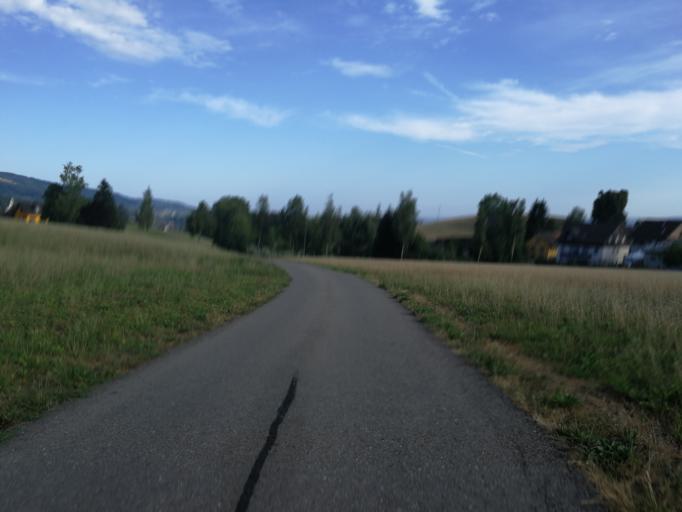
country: CH
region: Zurich
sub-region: Bezirk Meilen
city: Oetwil am See
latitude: 47.2641
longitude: 8.7349
